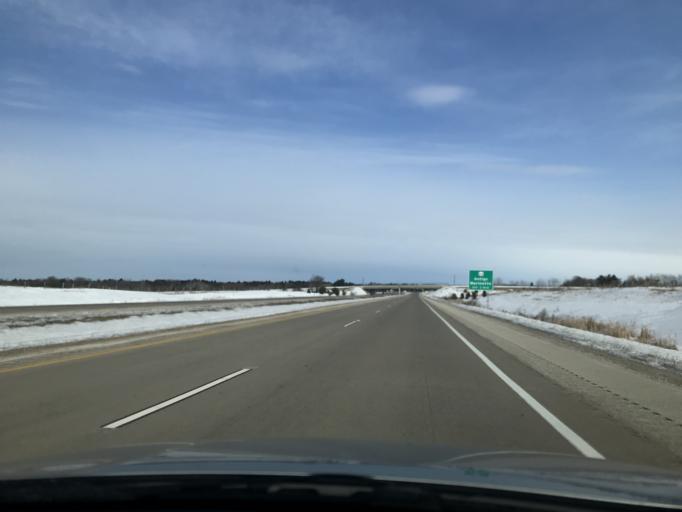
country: US
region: Wisconsin
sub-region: Oconto County
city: Oconto Falls
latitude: 45.0998
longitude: -88.0405
